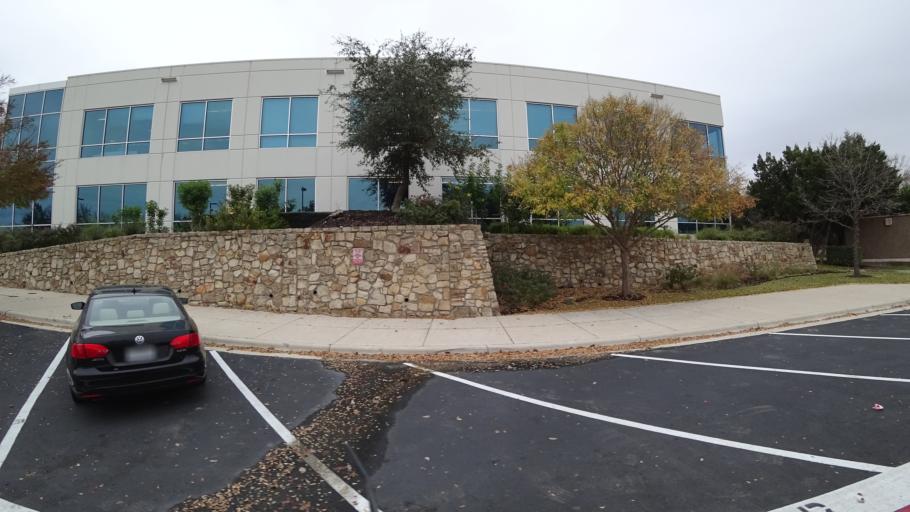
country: US
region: Texas
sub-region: Travis County
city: West Lake Hills
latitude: 30.3708
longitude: -97.8014
